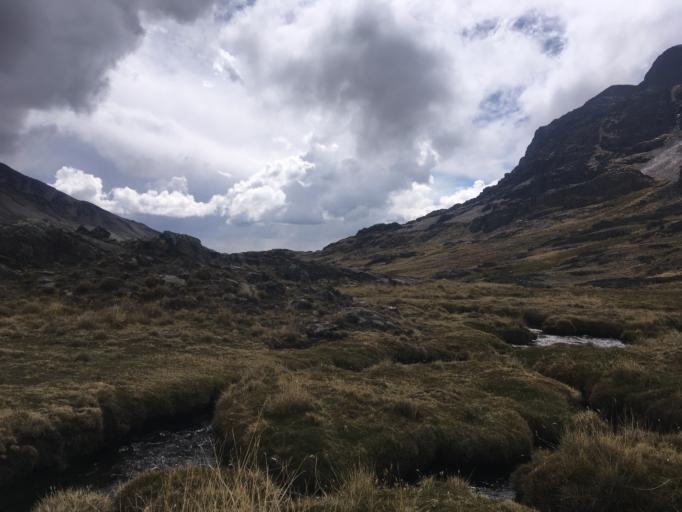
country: BO
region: La Paz
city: La Paz
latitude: -16.3927
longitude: -67.9638
